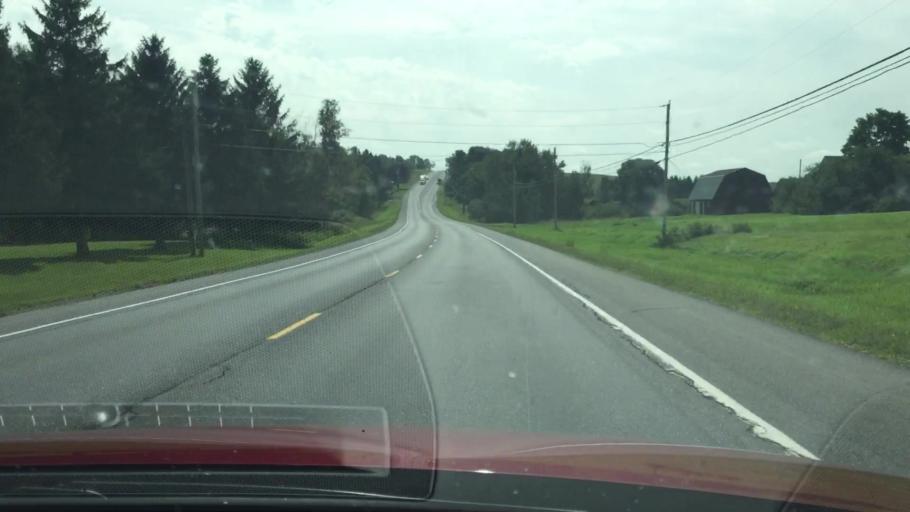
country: US
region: Maine
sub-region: Aroostook County
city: Easton
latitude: 46.5850
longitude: -67.9600
